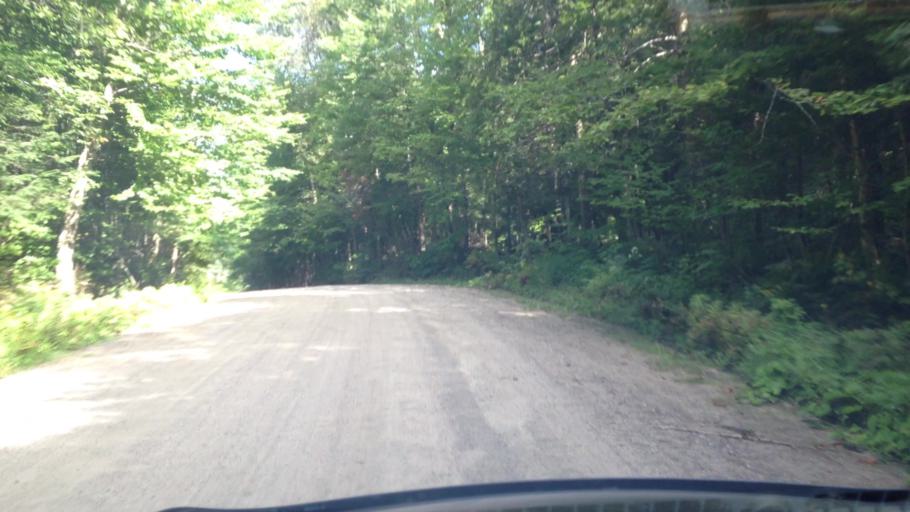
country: CA
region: Quebec
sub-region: Laurentides
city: Mont-Tremblant
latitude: 45.9267
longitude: -74.5833
